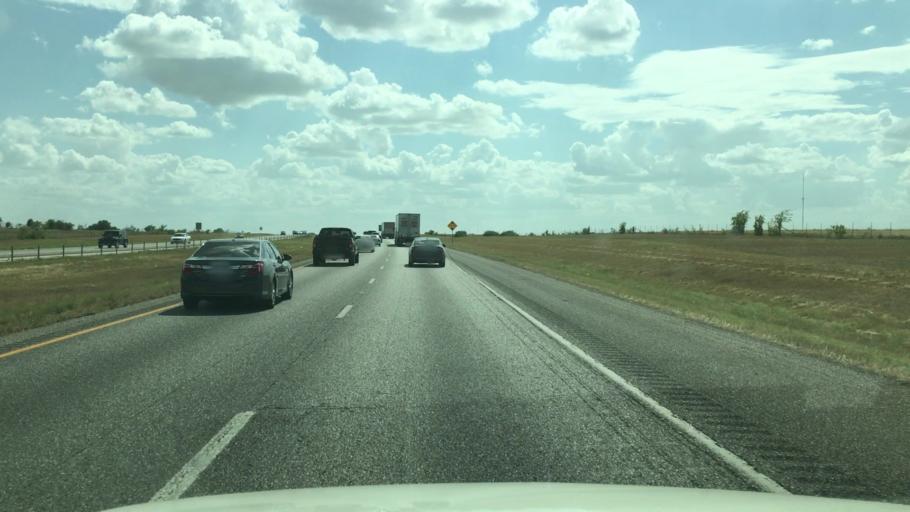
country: US
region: Texas
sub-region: Ellis County
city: Plum Grove
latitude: 32.1108
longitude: -96.9999
